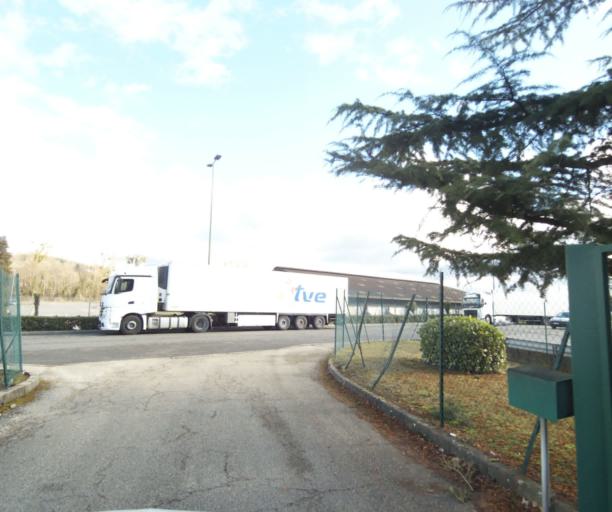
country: FR
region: Rhone-Alpes
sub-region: Departement de la Loire
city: La Talaudiere
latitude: 45.4745
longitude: 4.4236
